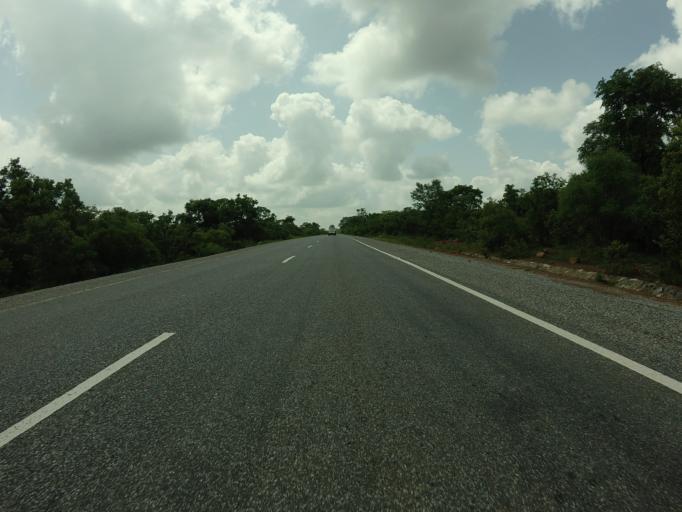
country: GH
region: Northern
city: Tamale
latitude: 9.1137
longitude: -1.6878
